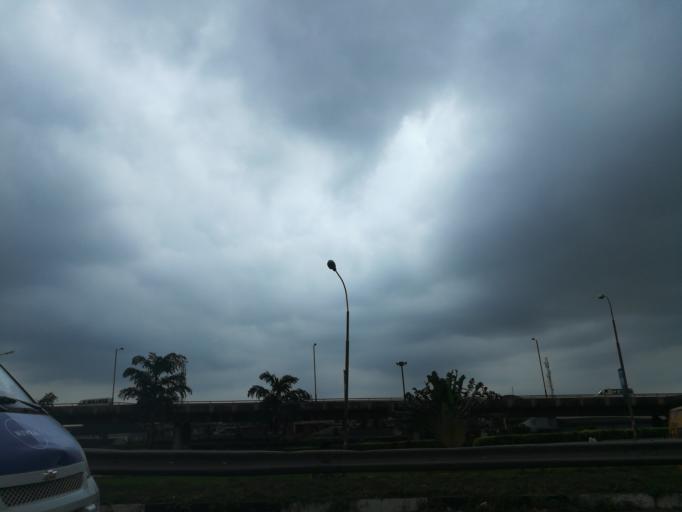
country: NG
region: Lagos
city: Somolu
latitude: 6.5486
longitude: 3.3968
